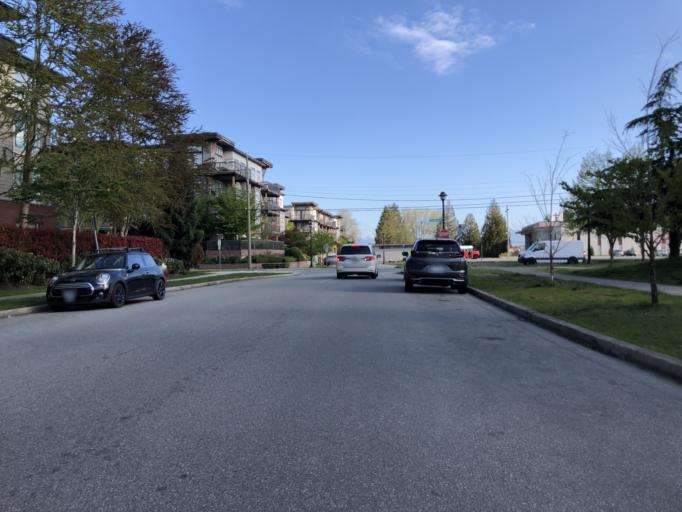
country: CA
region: British Columbia
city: Richmond
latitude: 49.1681
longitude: -123.1220
